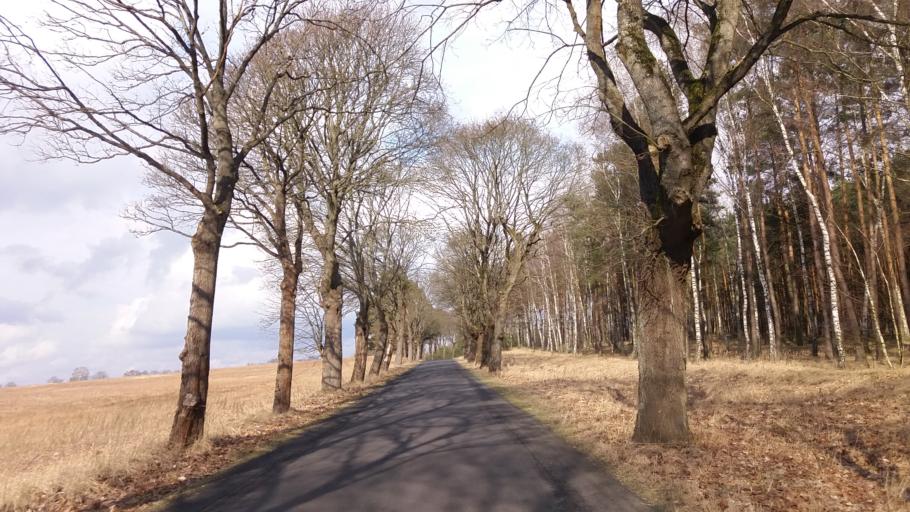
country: PL
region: West Pomeranian Voivodeship
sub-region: Powiat choszczenski
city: Drawno
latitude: 53.1654
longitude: 15.6858
